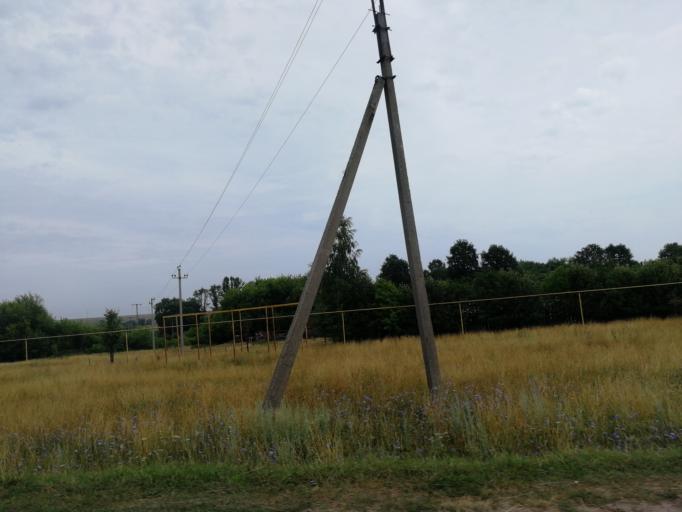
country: RU
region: Tula
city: Bogoroditsk
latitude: 53.7150
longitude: 38.1360
